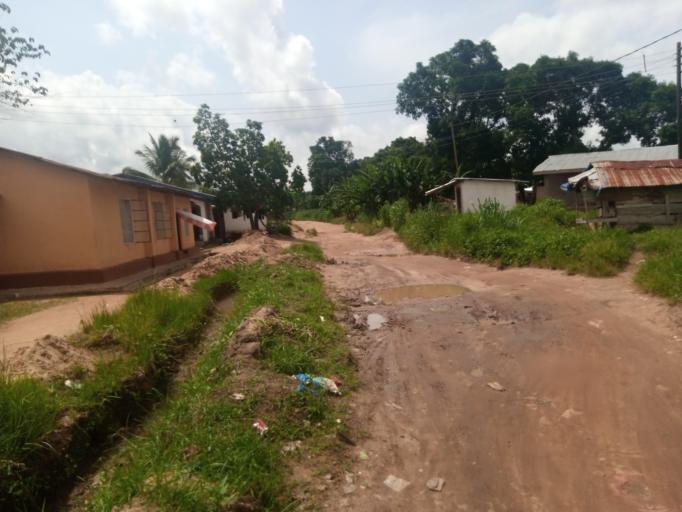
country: SL
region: Southern Province
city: Bo
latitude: 7.9623
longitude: -11.7526
